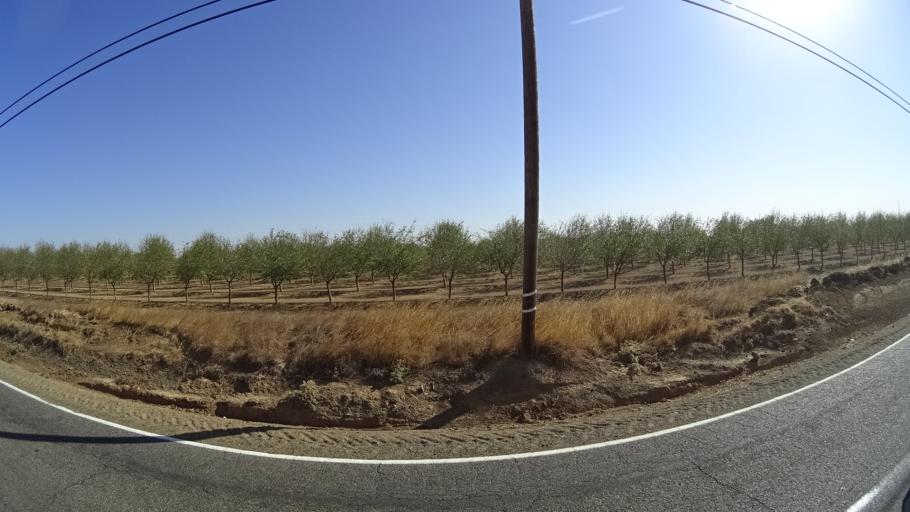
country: US
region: California
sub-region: Yolo County
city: Woodland
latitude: 38.6658
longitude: -121.8581
